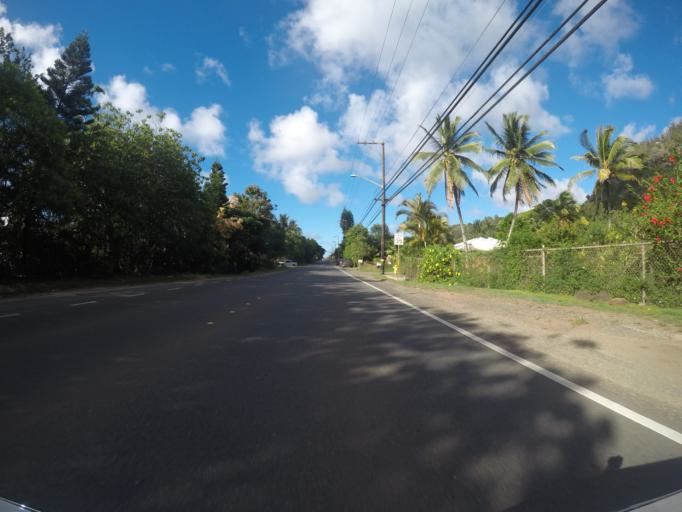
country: US
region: Hawaii
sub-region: Honolulu County
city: Pupukea
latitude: 21.6691
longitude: -158.0455
